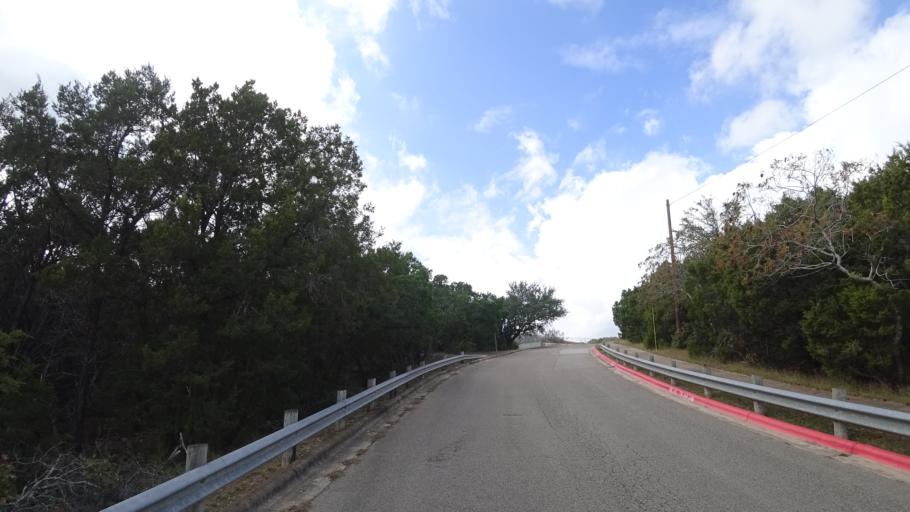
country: US
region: Texas
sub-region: Travis County
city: Barton Creek
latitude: 30.3053
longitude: -97.8823
